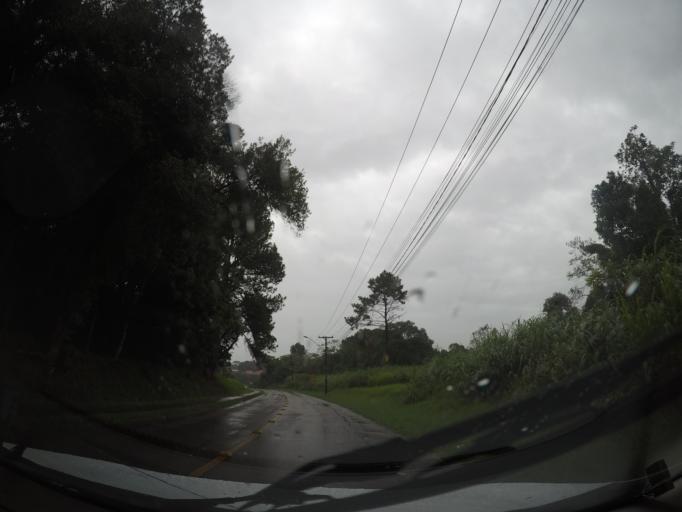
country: BR
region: Parana
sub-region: Curitiba
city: Curitiba
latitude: -25.4546
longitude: -49.3706
